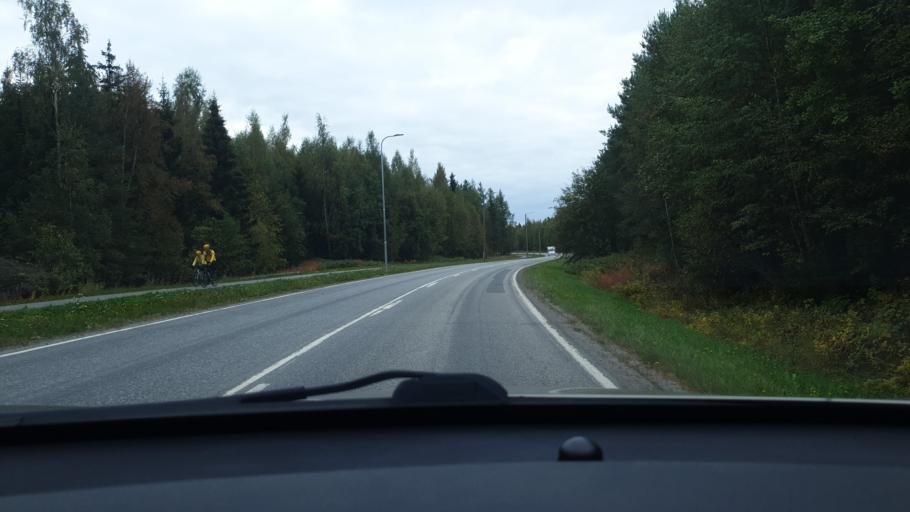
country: FI
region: Ostrobothnia
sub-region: Vaasa
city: Ristinummi
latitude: 63.0687
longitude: 21.7048
